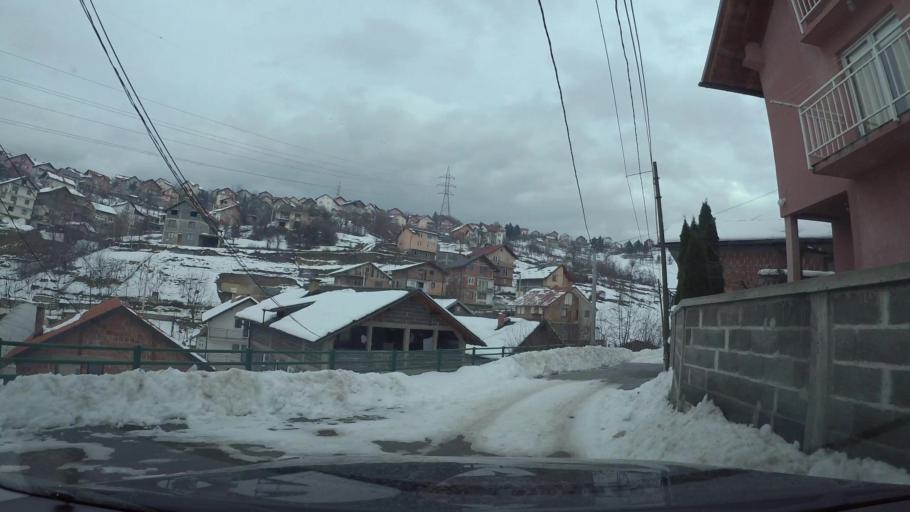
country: BA
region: Federation of Bosnia and Herzegovina
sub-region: Kanton Sarajevo
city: Sarajevo
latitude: 43.8593
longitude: 18.3329
